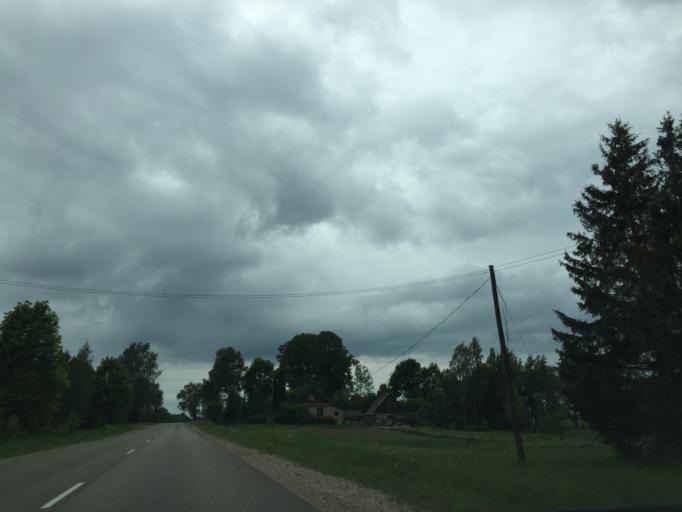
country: LV
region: Varkava
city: Vecvarkava
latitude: 56.0759
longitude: 26.6913
